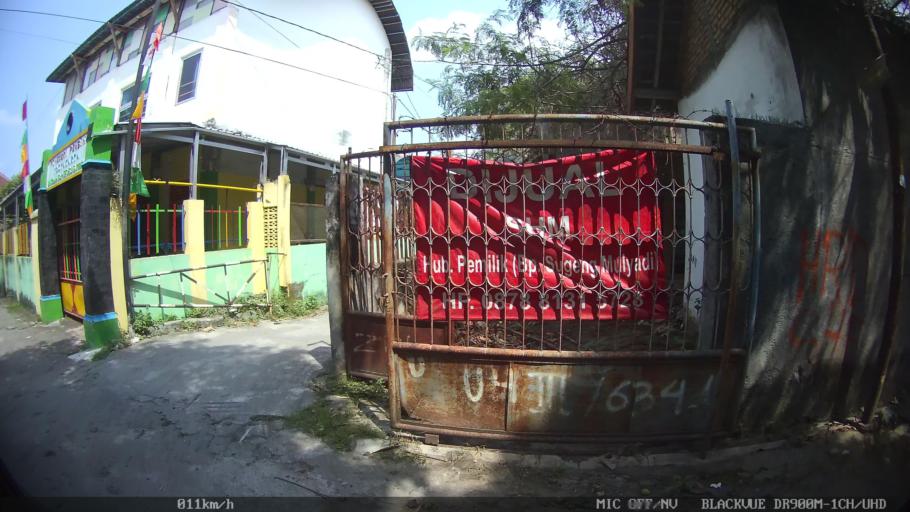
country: ID
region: Daerah Istimewa Yogyakarta
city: Yogyakarta
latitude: -7.8095
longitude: 110.3866
